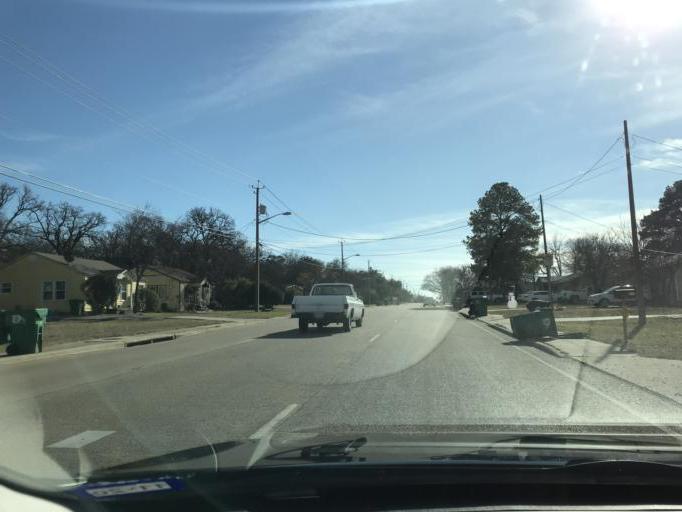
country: US
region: Texas
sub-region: Denton County
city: Denton
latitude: 33.2389
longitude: -97.1332
